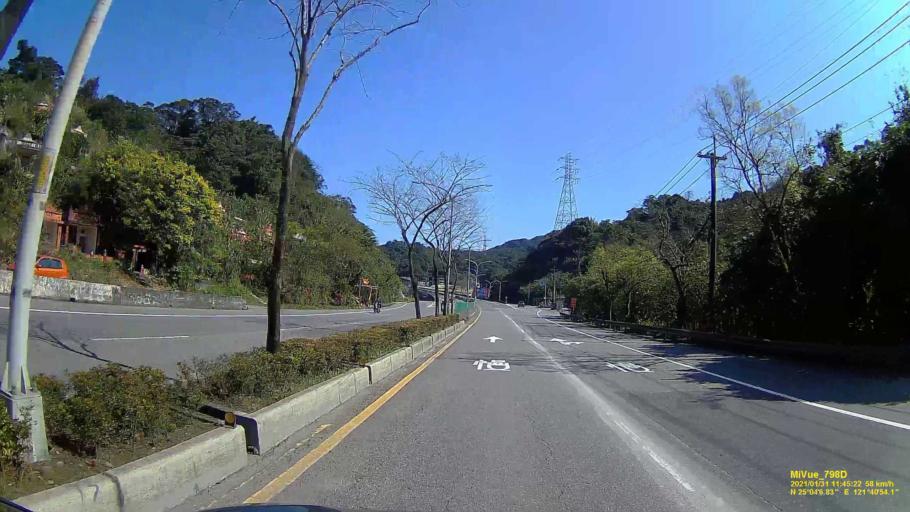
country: TW
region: Taiwan
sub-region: Keelung
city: Keelung
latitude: 25.0686
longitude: 121.6820
